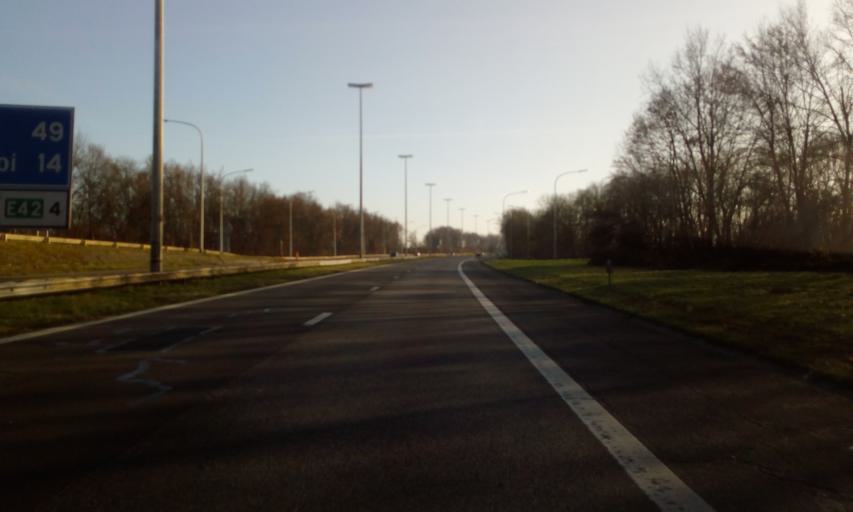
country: BE
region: Wallonia
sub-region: Province du Hainaut
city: Brunehault
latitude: 50.5138
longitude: 4.4097
